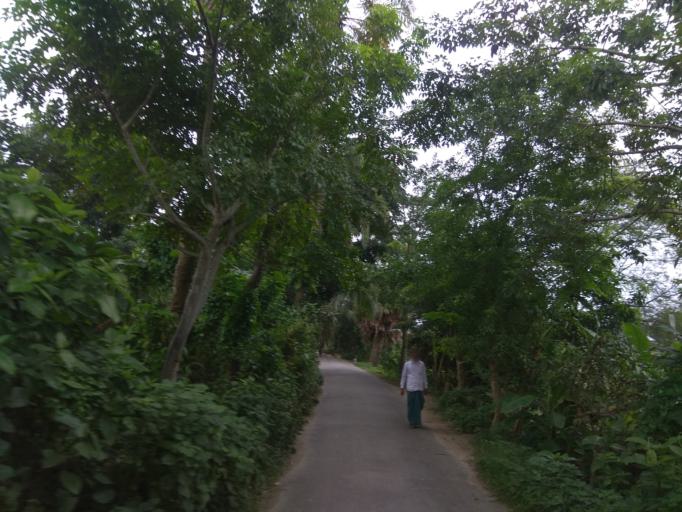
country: BD
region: Dhaka
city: Dohar
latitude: 23.4851
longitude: 89.9996
